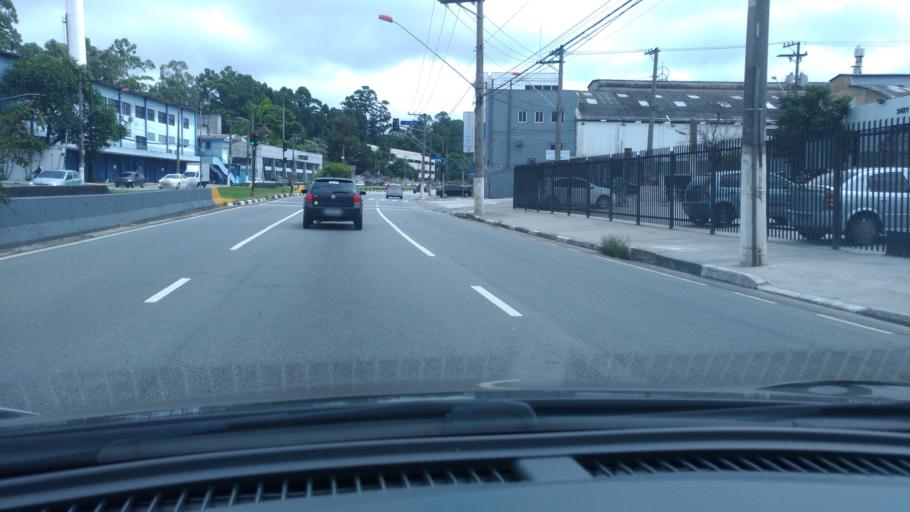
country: BR
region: Sao Paulo
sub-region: Diadema
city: Diadema
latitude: -23.6831
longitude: -46.6023
